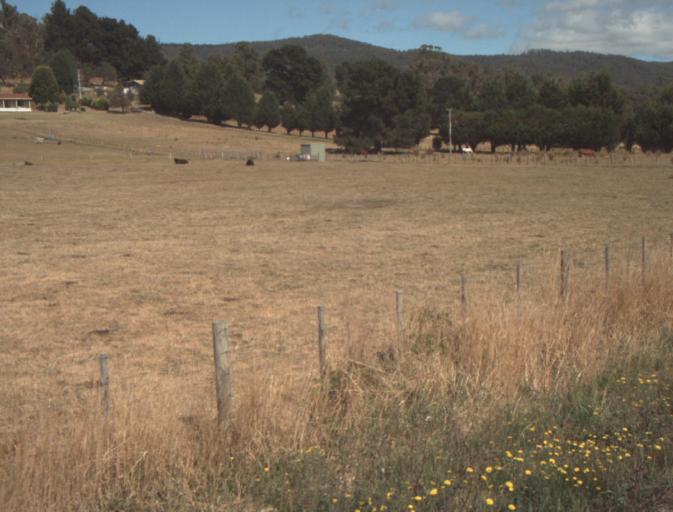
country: AU
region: Tasmania
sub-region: Launceston
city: Mayfield
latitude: -41.2592
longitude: 147.1551
